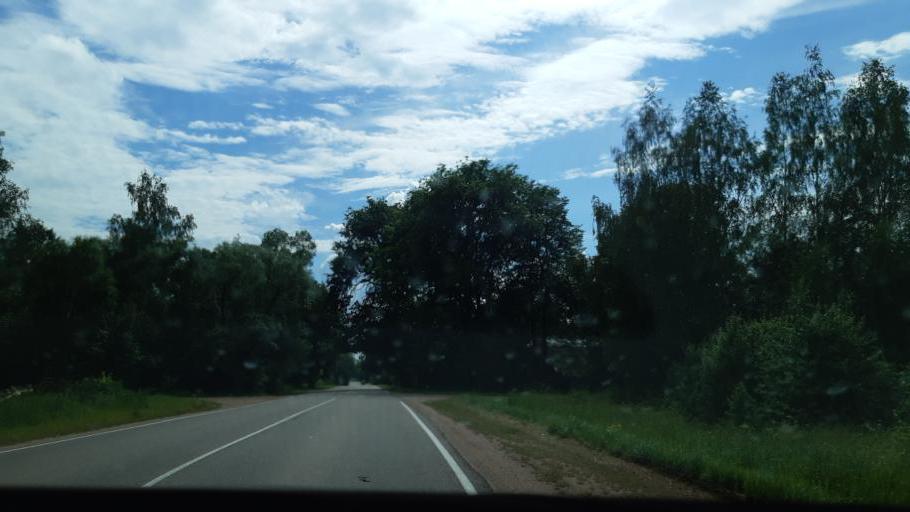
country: RU
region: Kaluga
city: Medyn'
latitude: 55.0642
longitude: 35.9132
